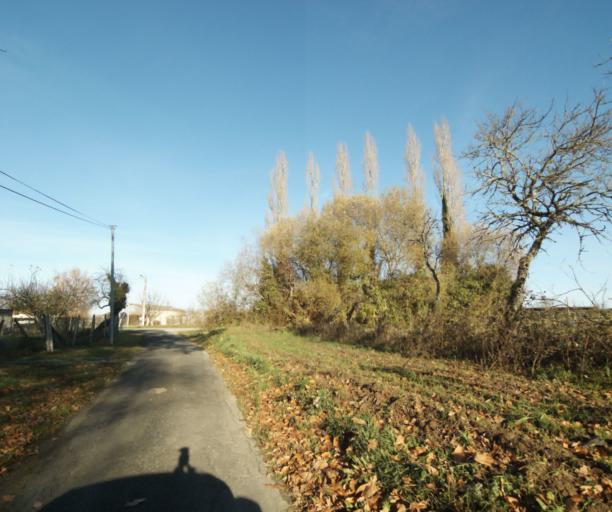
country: FR
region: Poitou-Charentes
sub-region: Departement de la Charente-Maritime
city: Cherac
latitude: 45.7298
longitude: -0.4752
